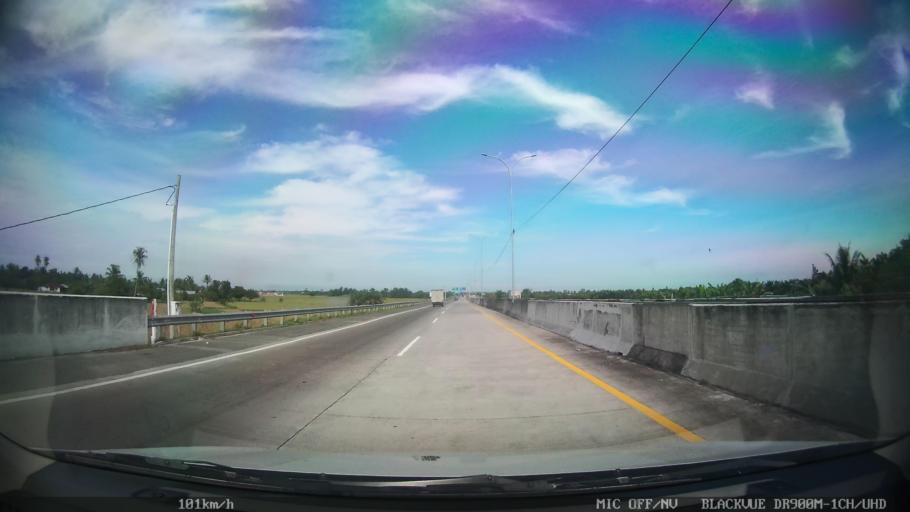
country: ID
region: North Sumatra
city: Sunggal
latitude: 3.6413
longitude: 98.5681
